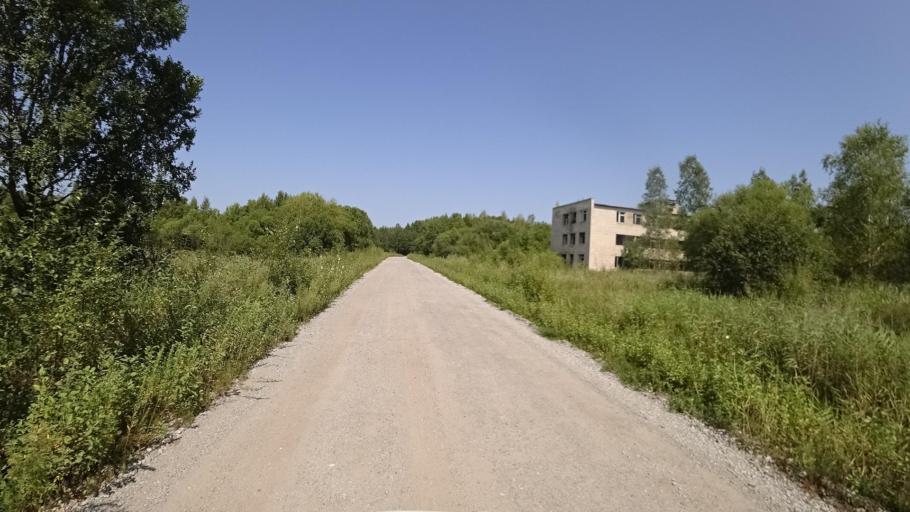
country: RU
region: Khabarovsk Krai
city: Khor
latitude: 47.9713
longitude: 135.1141
